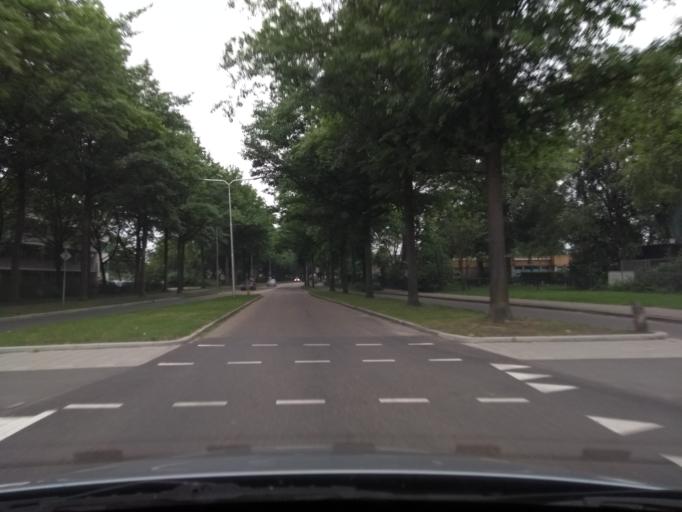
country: NL
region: Overijssel
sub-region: Gemeente Almelo
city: Almelo
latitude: 52.3727
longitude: 6.6784
